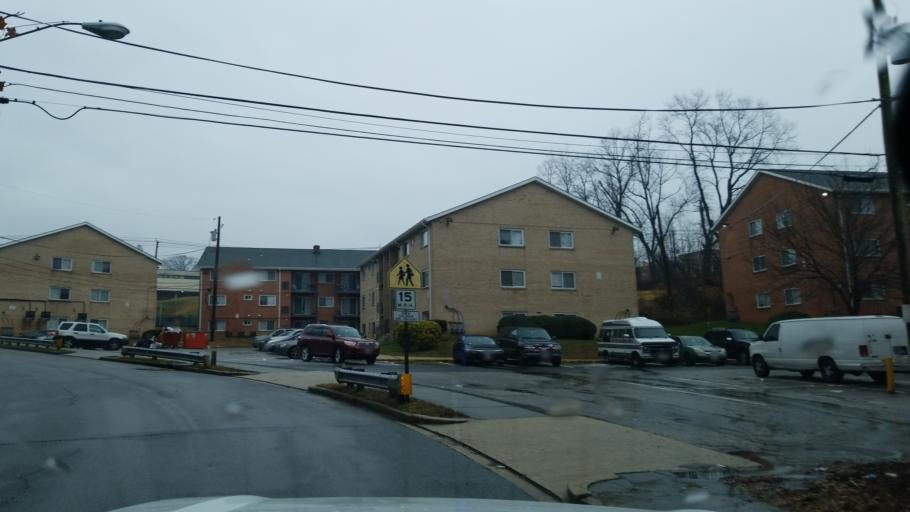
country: US
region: Maryland
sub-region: Prince George's County
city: Hillcrest Heights
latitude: 38.8552
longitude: -76.9879
